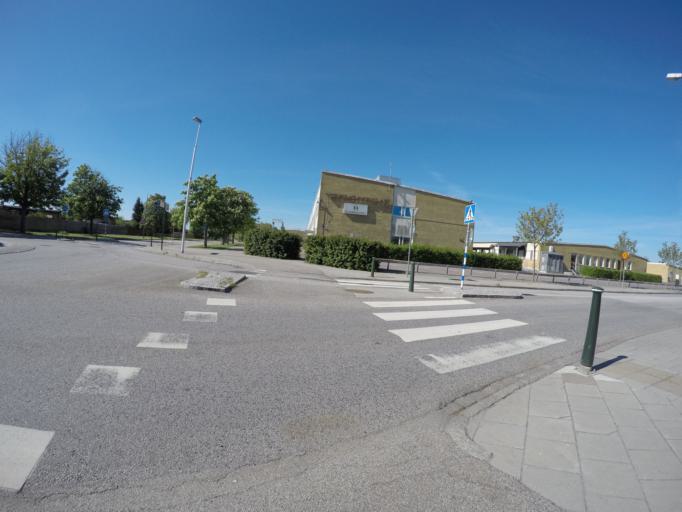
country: SE
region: Skane
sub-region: Burlovs Kommun
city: Arloev
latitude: 55.5912
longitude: 13.0716
